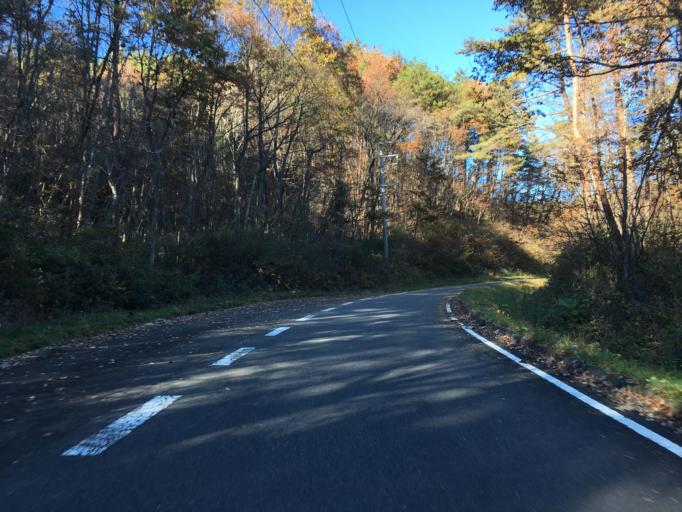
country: JP
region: Fukushima
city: Ishikawa
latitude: 37.2377
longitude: 140.5232
